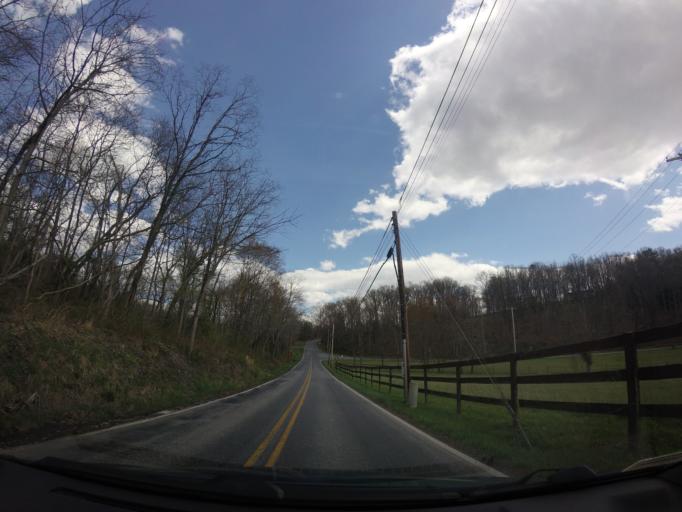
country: US
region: Maryland
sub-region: Washington County
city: Keedysville
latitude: 39.4399
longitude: -77.6835
